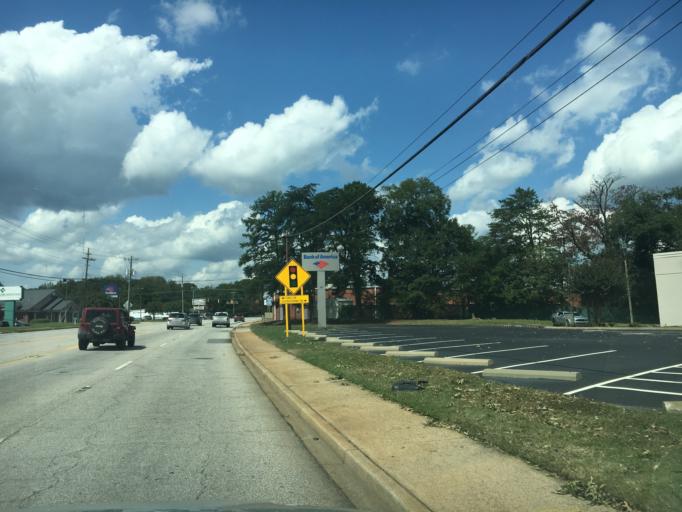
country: US
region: South Carolina
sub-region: Greenville County
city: Berea
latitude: 34.8835
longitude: -82.4564
